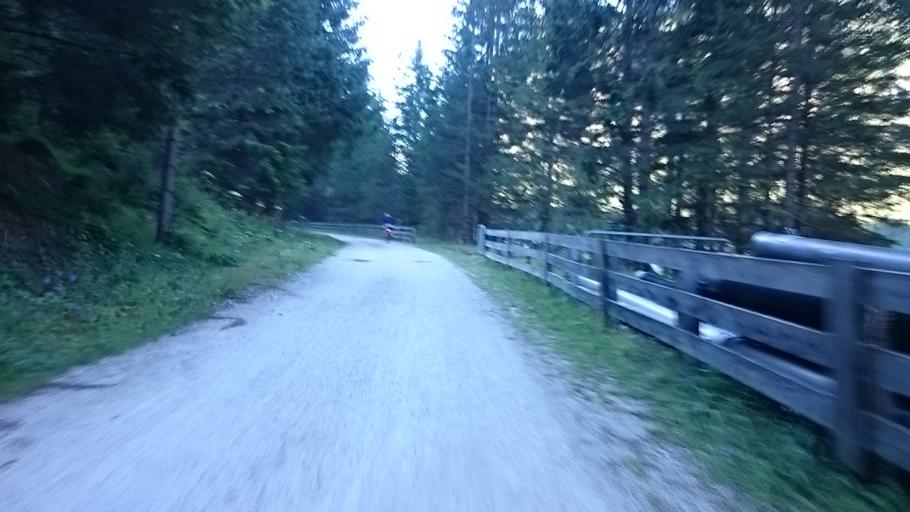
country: IT
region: Trentino-Alto Adige
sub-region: Bolzano
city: Dobbiaco
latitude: 46.7023
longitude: 12.2218
